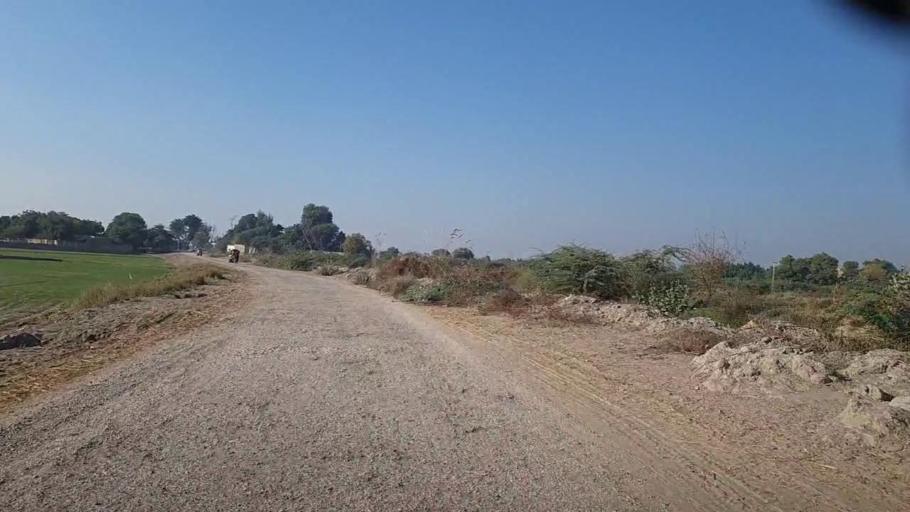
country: PK
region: Sindh
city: Darya Khan Marri
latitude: 26.6940
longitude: 68.3482
